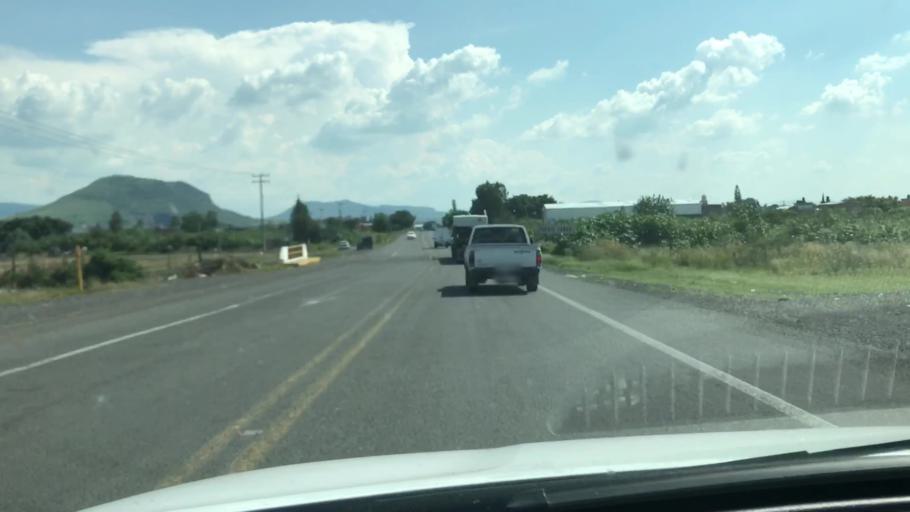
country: MX
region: Michoacan
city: Tanhuato de Guerrero
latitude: 20.2917
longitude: -102.3355
